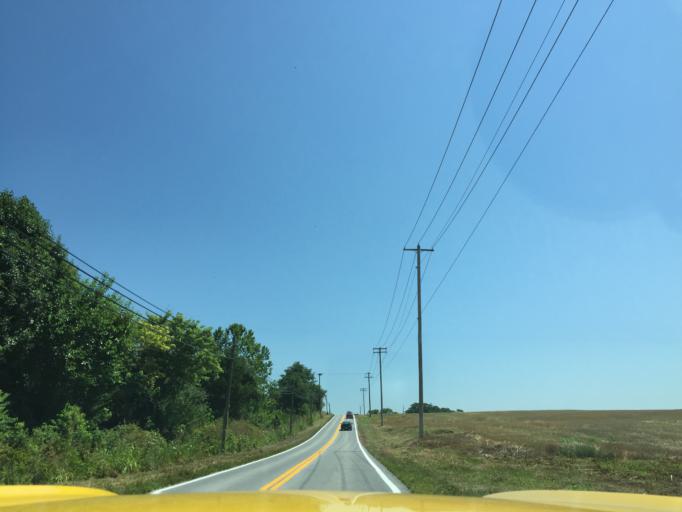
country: US
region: West Virginia
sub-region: Jefferson County
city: Ranson
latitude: 39.2987
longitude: -77.8272
